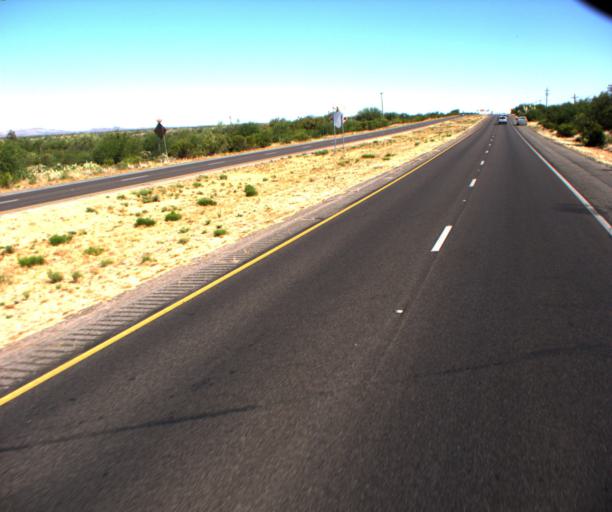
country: US
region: Arizona
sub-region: Pima County
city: Catalina
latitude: 32.5144
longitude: -110.9258
